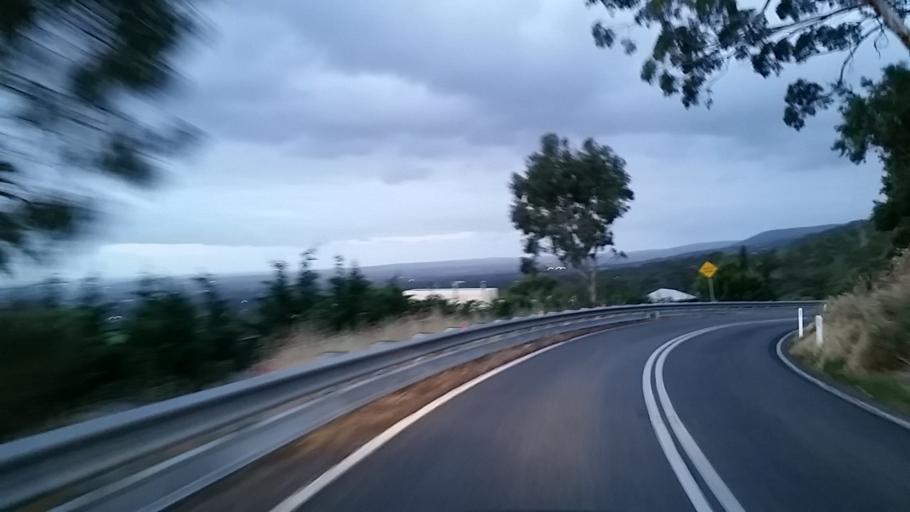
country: AU
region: South Australia
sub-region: Burnside
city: Beaumont
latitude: -34.9455
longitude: 138.6705
